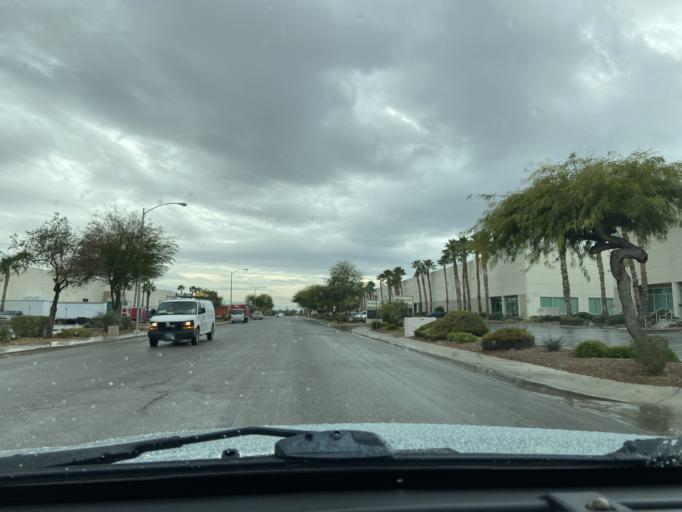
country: US
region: Nevada
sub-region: Clark County
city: Sunrise Manor
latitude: 36.2347
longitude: -115.1034
